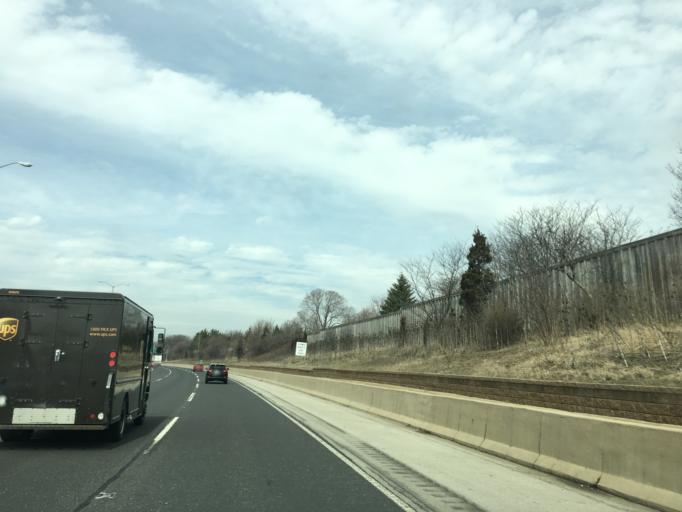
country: US
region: Illinois
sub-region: DuPage County
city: Woodridge
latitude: 41.7617
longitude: -88.0362
